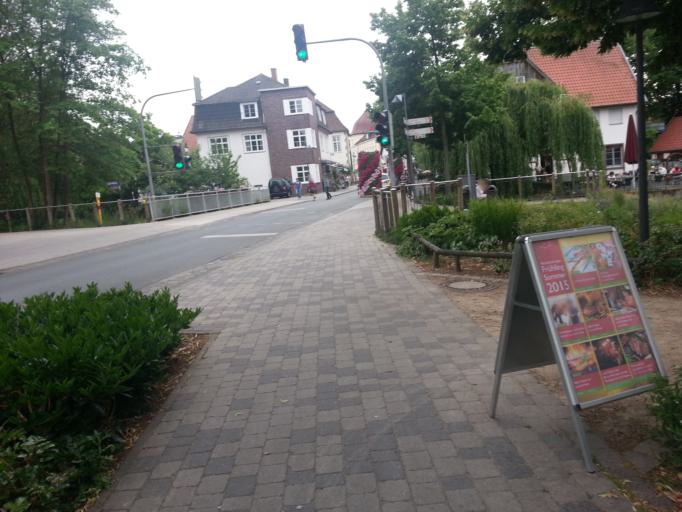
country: DE
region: North Rhine-Westphalia
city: Rietberg
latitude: 51.8107
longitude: 8.4281
